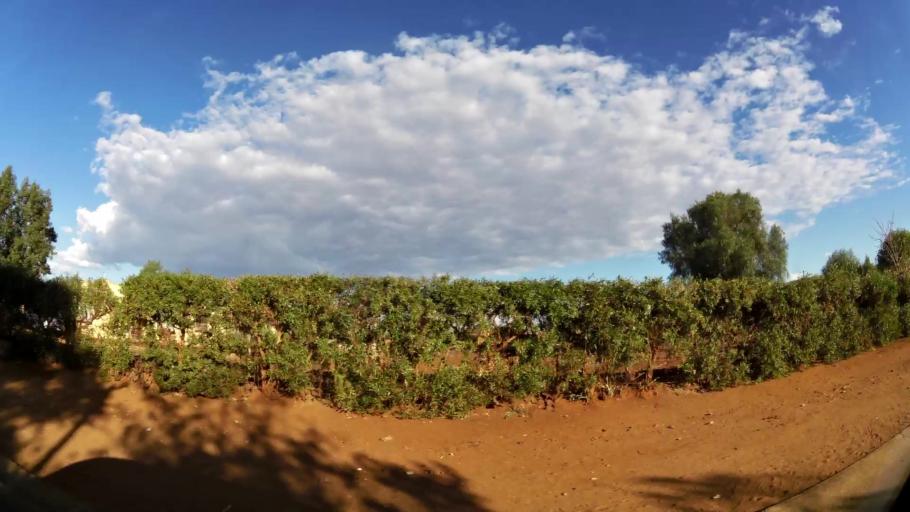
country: ZA
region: Limpopo
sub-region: Waterberg District Municipality
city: Mokopane
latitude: -24.1721
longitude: 28.9770
